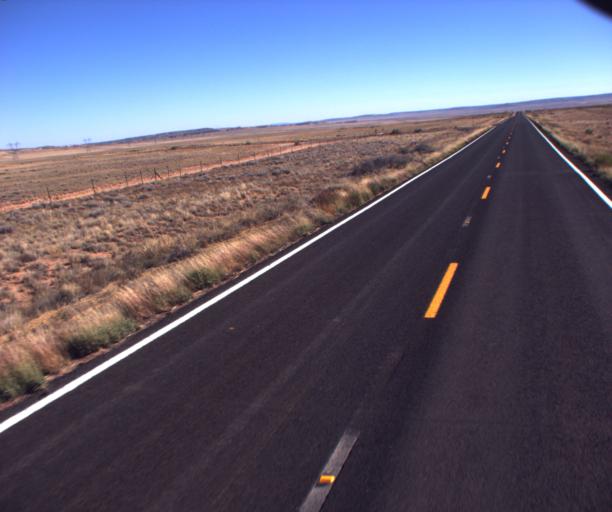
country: US
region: Arizona
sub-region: Coconino County
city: Tuba City
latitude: 35.9712
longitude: -110.8314
